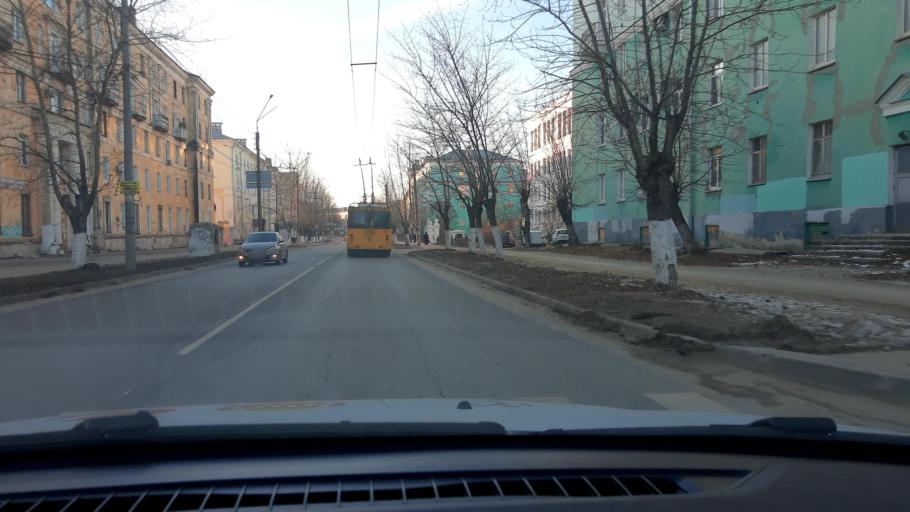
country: RU
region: Nizjnij Novgorod
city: Dzerzhinsk
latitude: 56.2420
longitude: 43.4528
